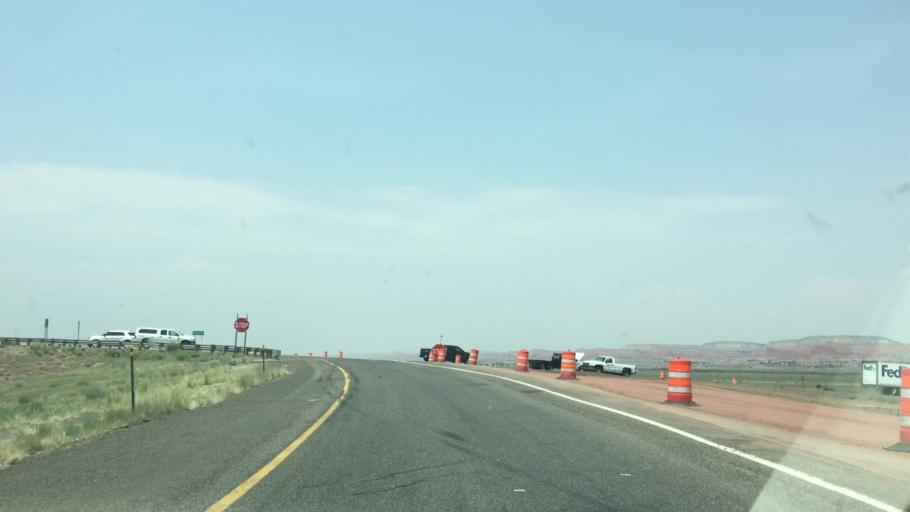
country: US
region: New Mexico
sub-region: McKinley County
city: Church Rock
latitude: 35.4807
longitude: -108.4358
